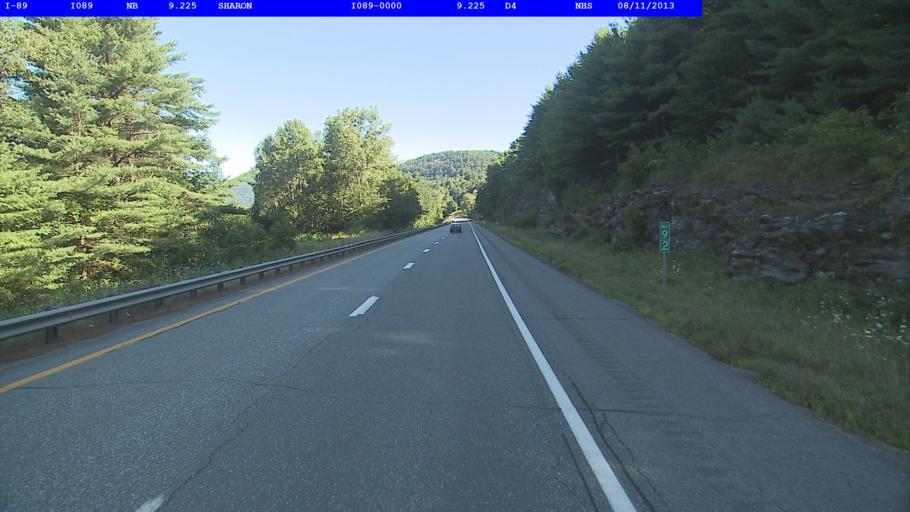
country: US
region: Vermont
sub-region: Windsor County
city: Wilder
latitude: 43.7310
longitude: -72.4311
